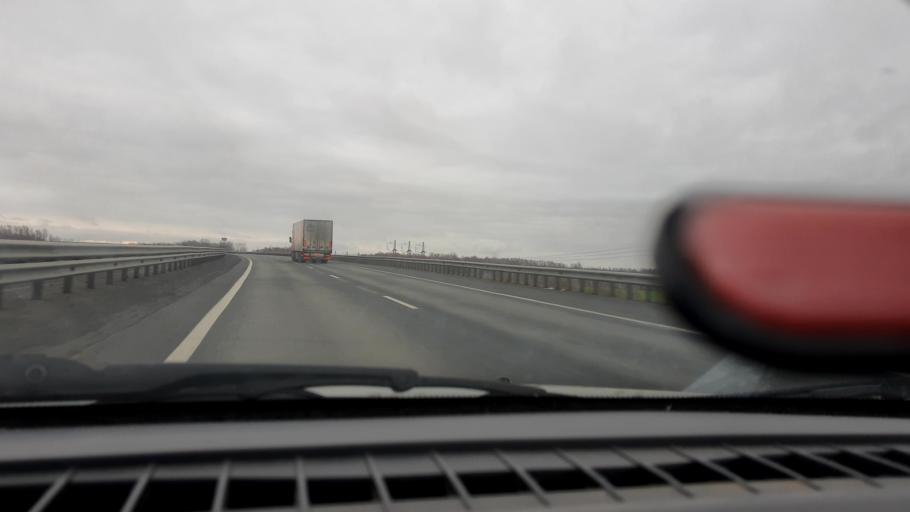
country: RU
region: Nizjnij Novgorod
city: Burevestnik
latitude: 56.1157
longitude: 43.8270
